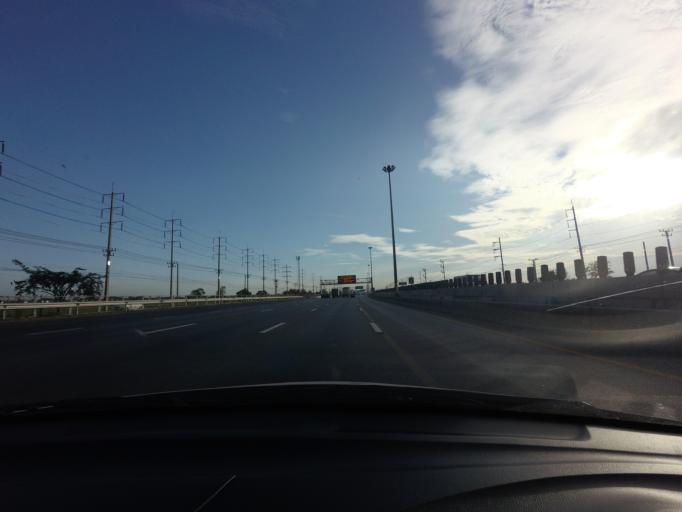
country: TH
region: Pathum Thani
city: Lam Luk Ka
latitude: 13.9490
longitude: 100.7124
